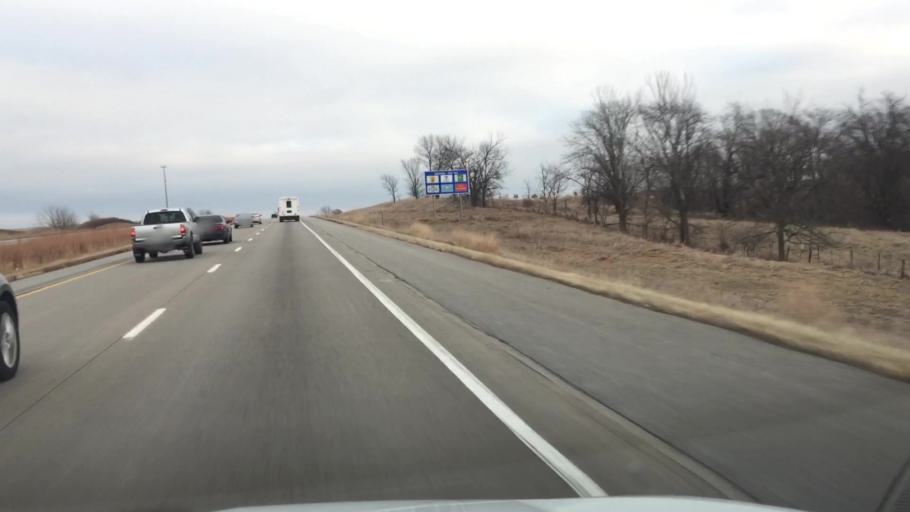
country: US
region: Iowa
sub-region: Jasper County
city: Colfax
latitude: 41.6834
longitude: -93.1489
